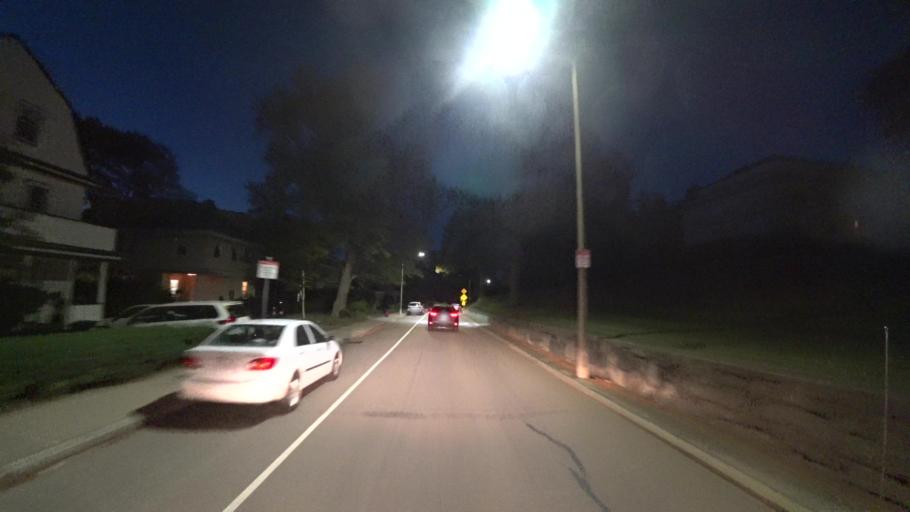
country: US
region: Massachusetts
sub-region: Middlesex County
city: Watertown
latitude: 42.3408
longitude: -71.1661
